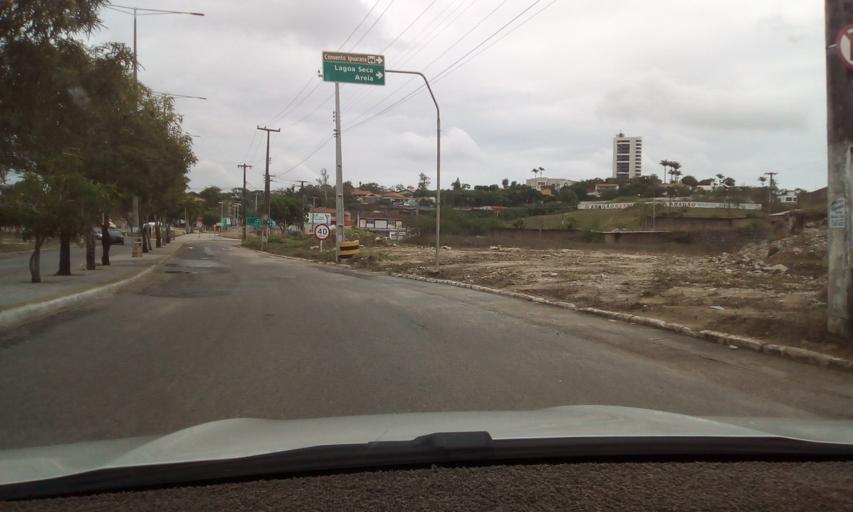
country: BR
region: Paraiba
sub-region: Campina Grande
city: Campina Grande
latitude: -7.1988
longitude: -35.8771
